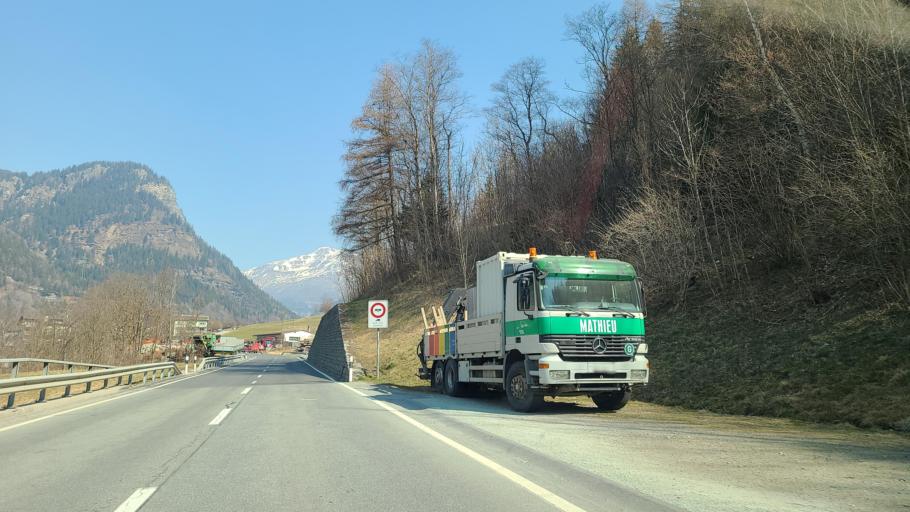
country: CH
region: Grisons
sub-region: Bernina District
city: Poschiavo
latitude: 46.3357
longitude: 10.0612
